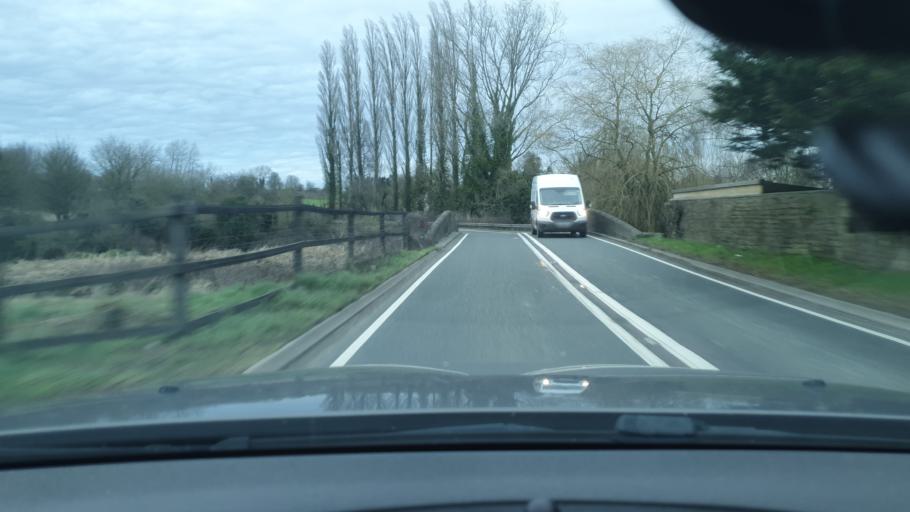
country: GB
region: England
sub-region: Wiltshire
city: Seend
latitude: 51.3377
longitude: -2.1070
